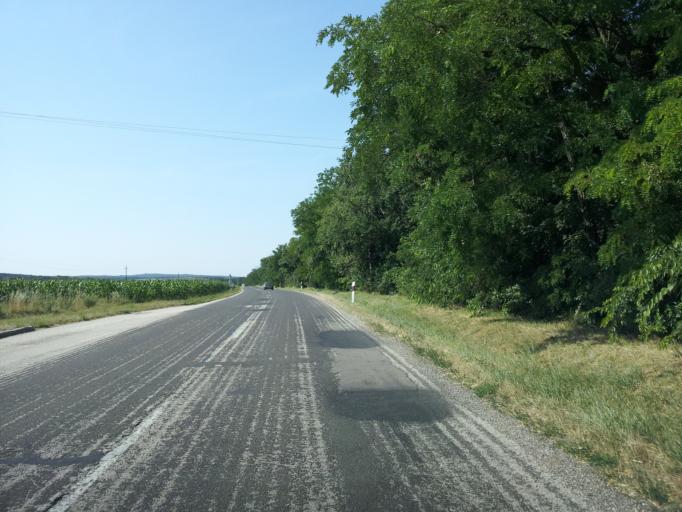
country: HU
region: Fejer
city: Lovasbereny
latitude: 47.2838
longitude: 18.5279
